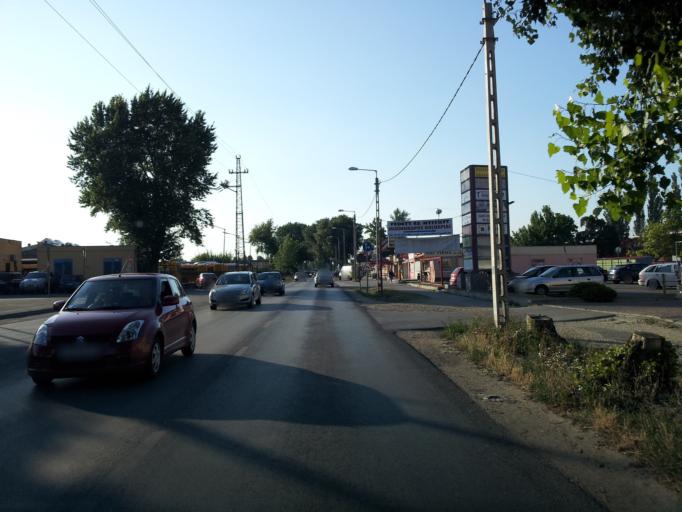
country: HU
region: Pest
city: Szigethalom
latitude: 47.3316
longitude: 19.0035
